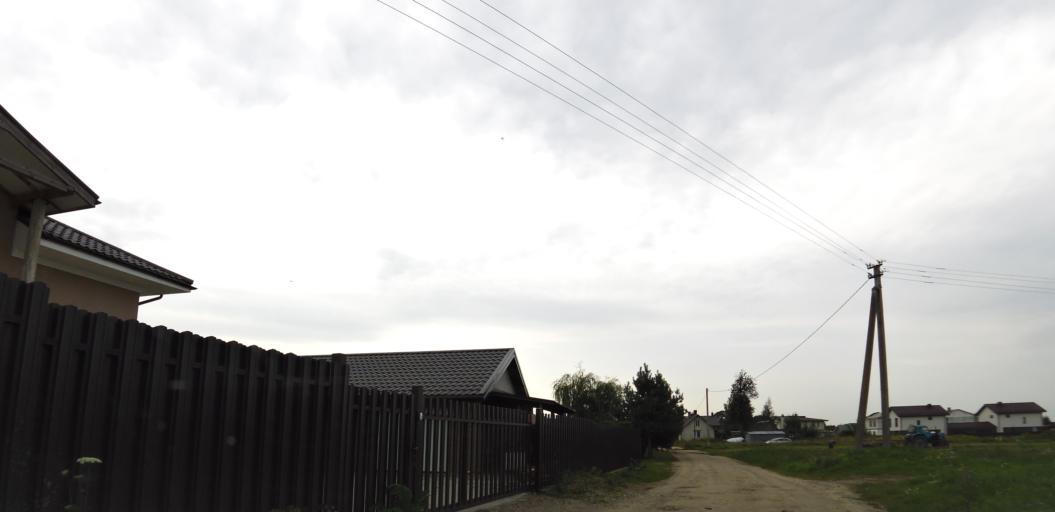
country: LT
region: Vilnius County
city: Pasilaiciai
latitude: 54.7607
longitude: 25.2301
